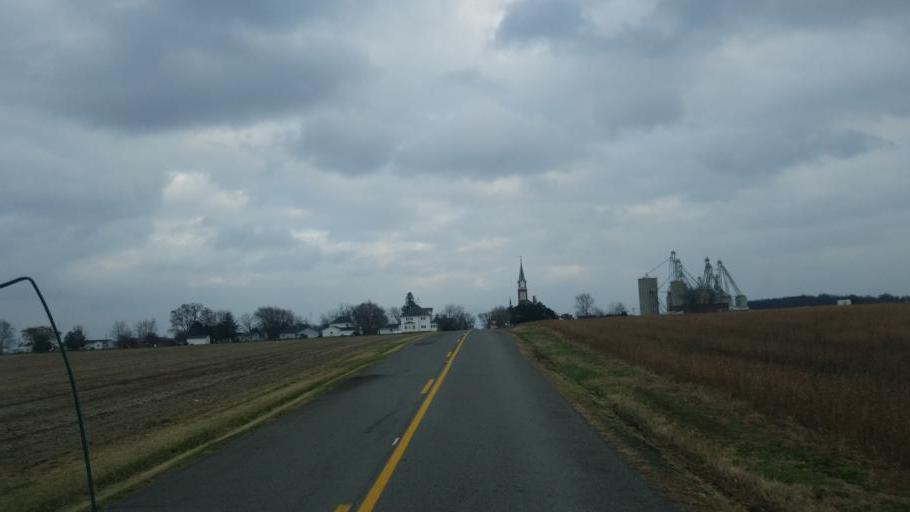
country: US
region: Ohio
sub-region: Mercer County
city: Fort Recovery
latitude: 40.5091
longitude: -84.7891
